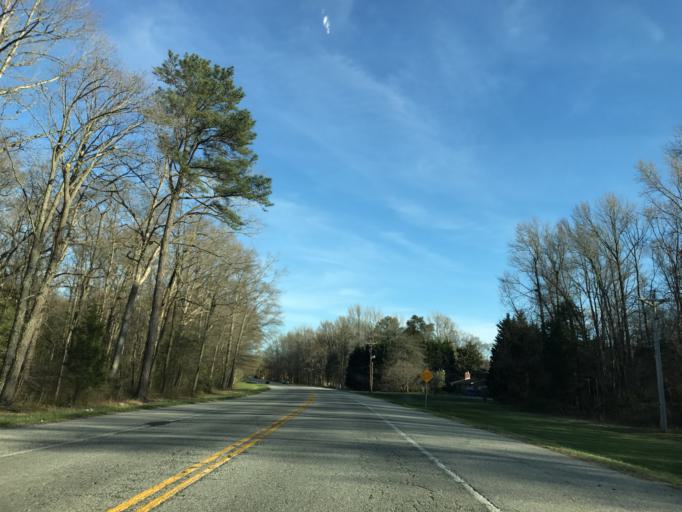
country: US
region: Maryland
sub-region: Caroline County
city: Greensboro
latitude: 39.1191
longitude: -75.7593
